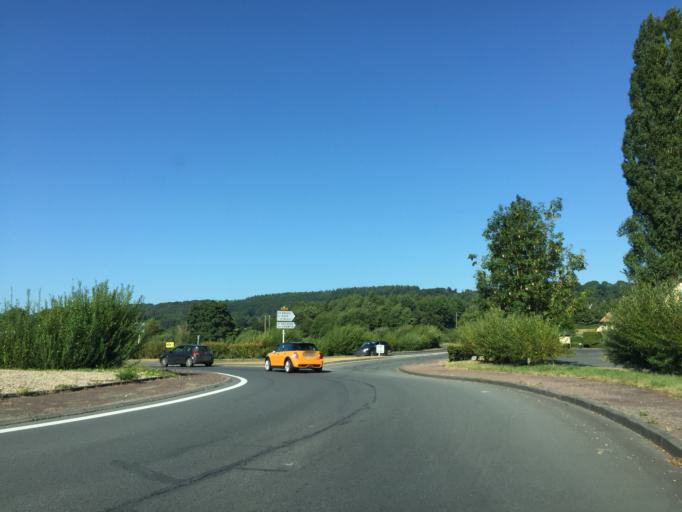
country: FR
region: Lower Normandy
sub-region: Departement du Calvados
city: Lisieux
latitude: 49.2296
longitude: 0.2184
